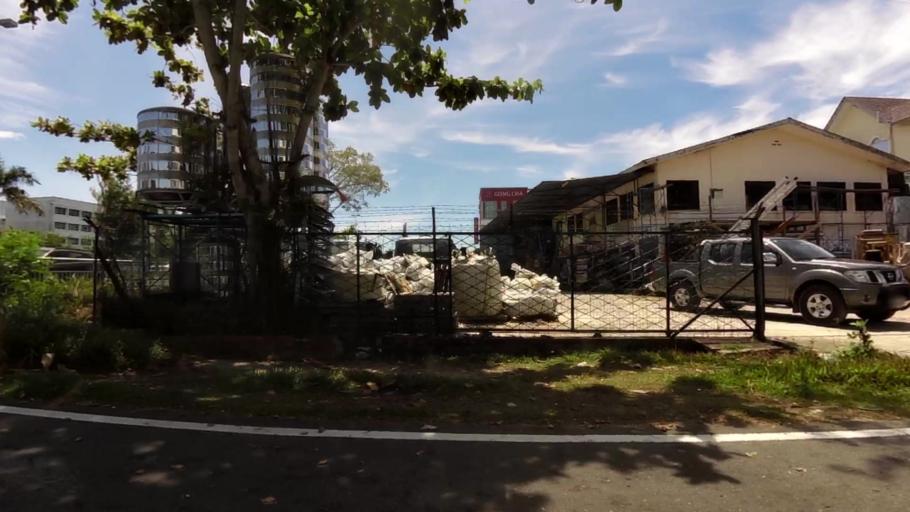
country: BN
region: Brunei and Muara
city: Bandar Seri Begawan
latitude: 4.9448
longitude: 114.9487
